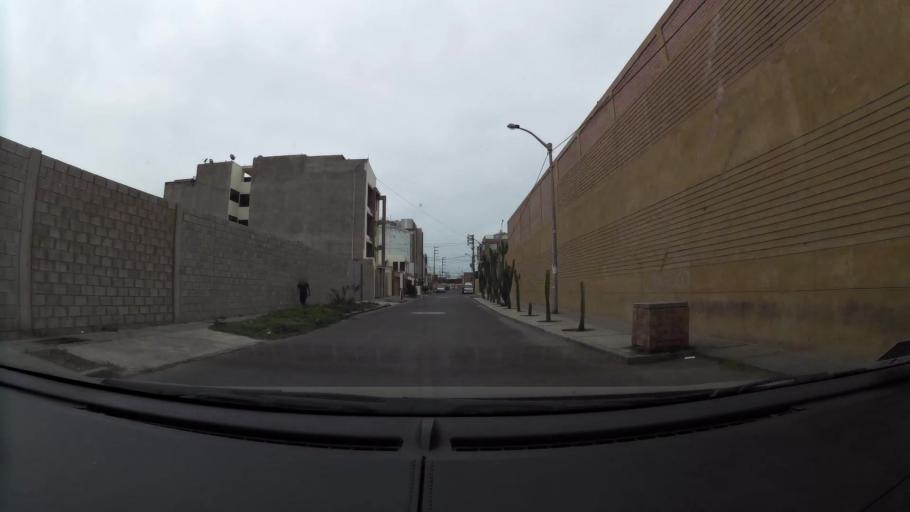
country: PE
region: La Libertad
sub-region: Provincia de Trujillo
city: Buenos Aires
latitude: -8.1373
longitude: -79.0361
